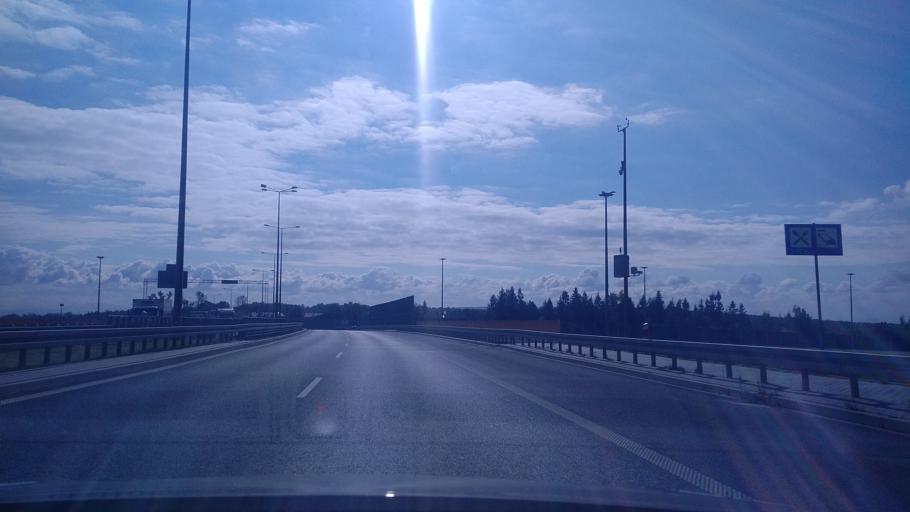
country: PL
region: Lesser Poland Voivodeship
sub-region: Powiat krakowski
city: Modlnica
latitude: 50.1200
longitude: 19.8684
